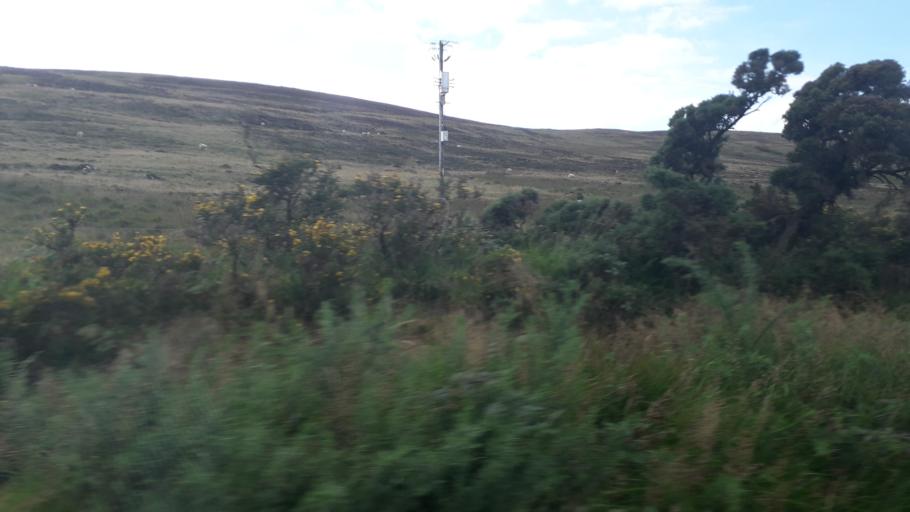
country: GB
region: Northern Ireland
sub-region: Down District
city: Warrenpoint
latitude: 54.0442
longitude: -6.2697
